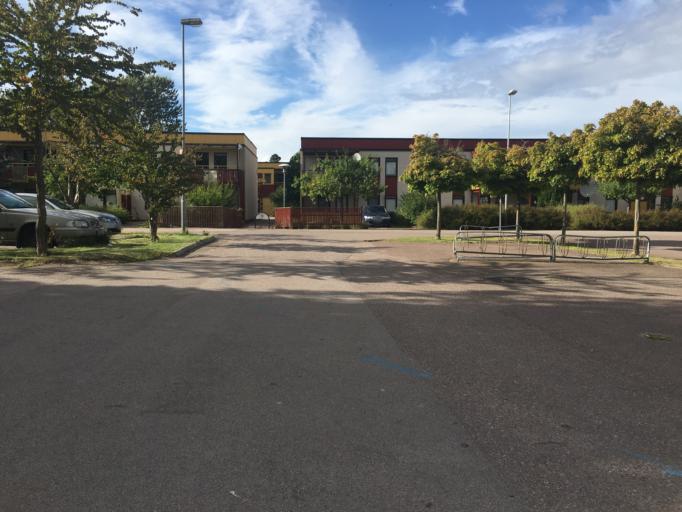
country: SE
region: Kalmar
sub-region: Kalmar Kommun
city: Kalmar
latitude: 56.7035
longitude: 16.3574
